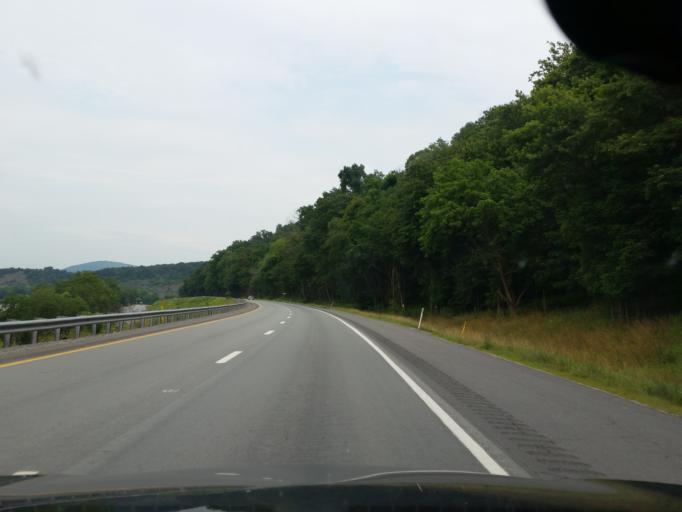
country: US
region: Pennsylvania
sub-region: Perry County
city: Duncannon
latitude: 40.4739
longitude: -77.0344
